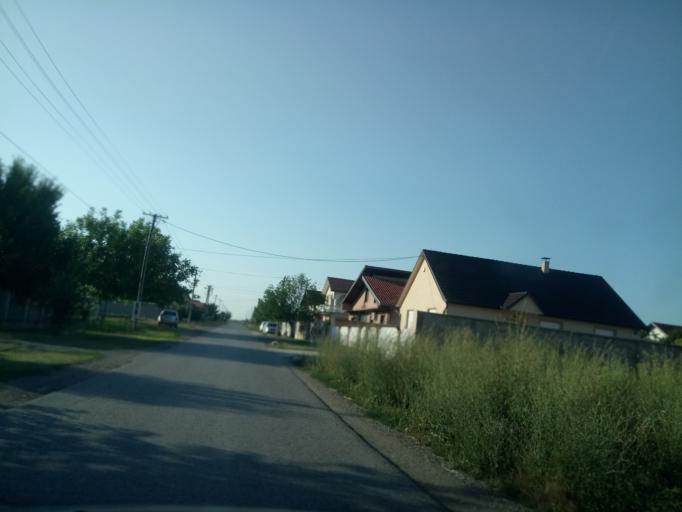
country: RS
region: Autonomna Pokrajina Vojvodina
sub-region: Sremski Okrug
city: Stara Pazova
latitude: 44.9927
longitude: 20.1687
